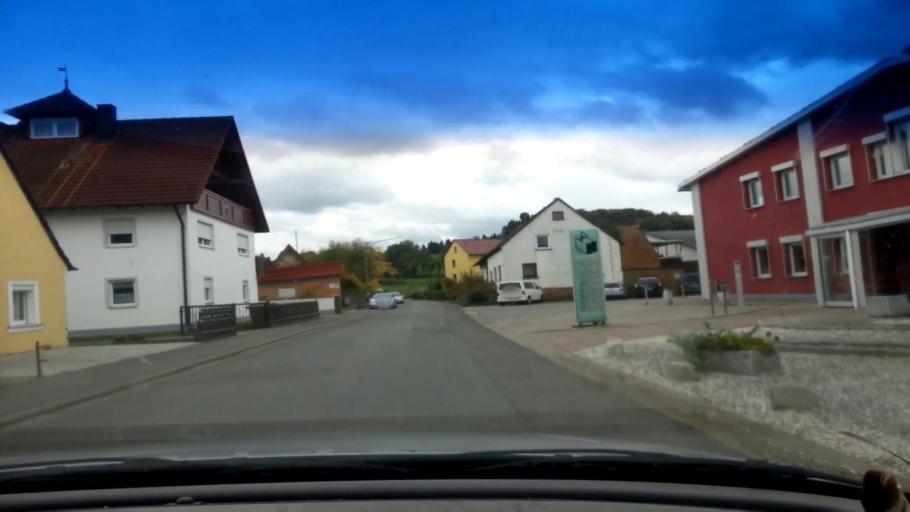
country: DE
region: Bavaria
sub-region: Upper Franconia
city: Priesendorf
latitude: 49.8999
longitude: 10.7138
